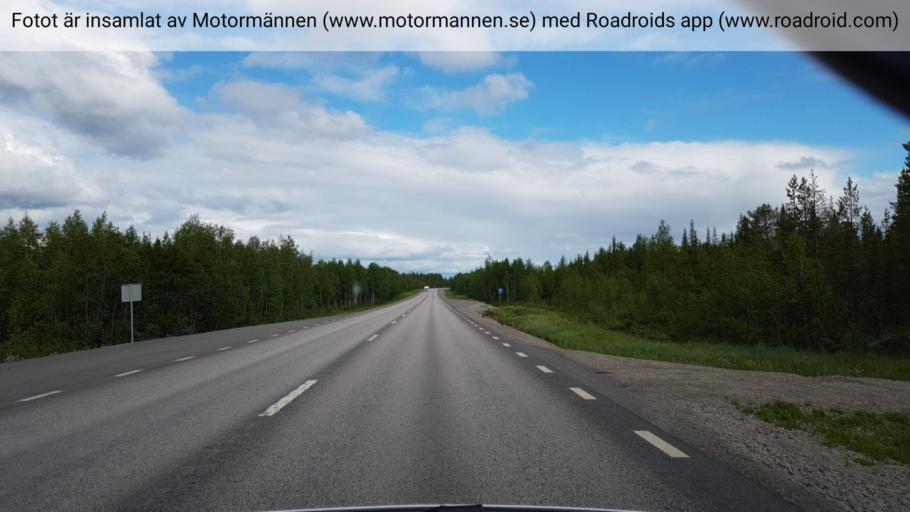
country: SE
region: Norrbotten
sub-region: Gallivare Kommun
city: Malmberget
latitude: 67.6628
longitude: 21.4788
